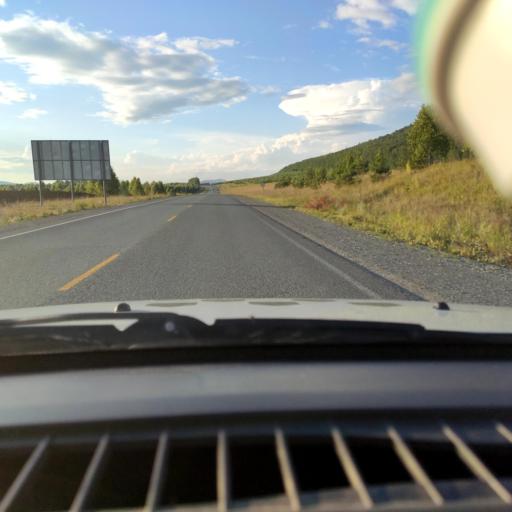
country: RU
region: Chelyabinsk
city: Karabash
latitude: 55.3440
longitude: 60.2450
